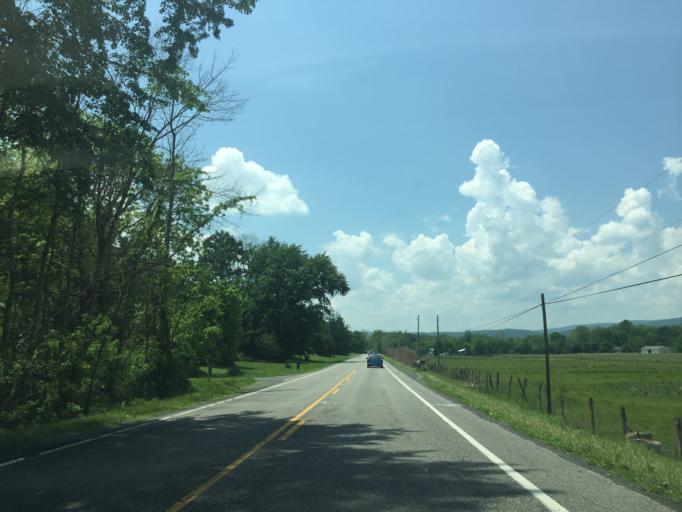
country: US
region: Virginia
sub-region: Shenandoah County
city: Woodstock
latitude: 39.0918
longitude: -78.5759
